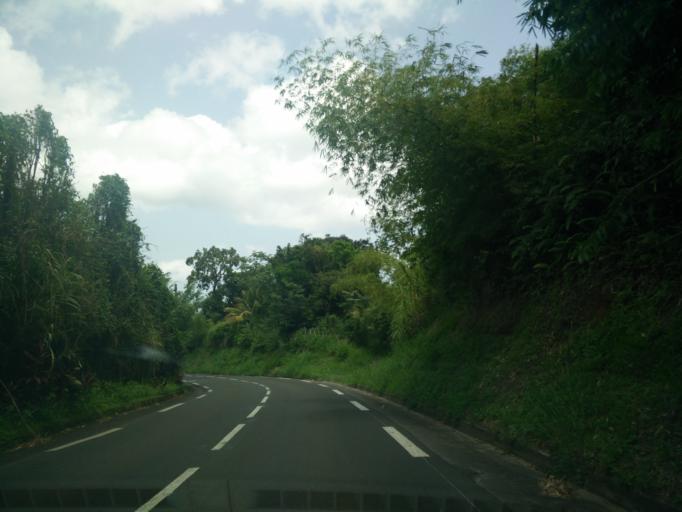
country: MQ
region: Martinique
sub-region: Martinique
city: Le Morne-Rouge
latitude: 14.7628
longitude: -61.1551
